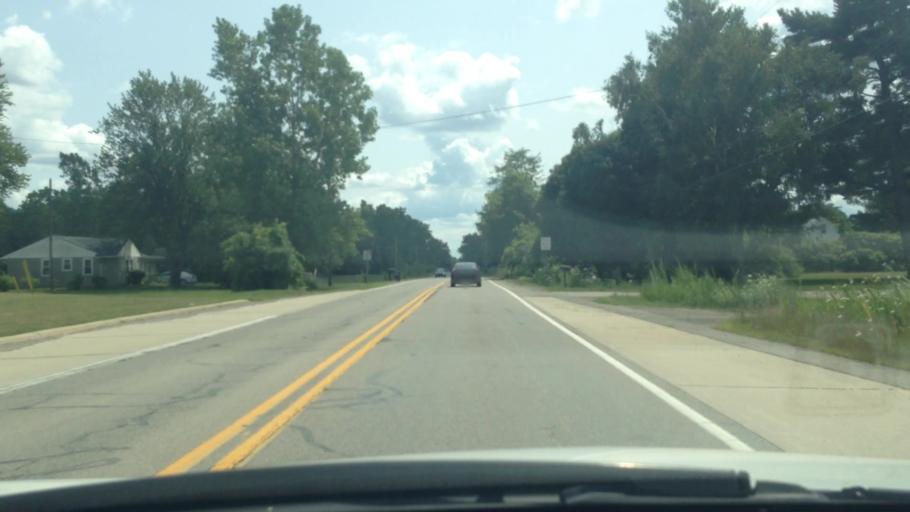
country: US
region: Michigan
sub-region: Wayne County
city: Taylor
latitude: 42.2050
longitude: -83.3069
